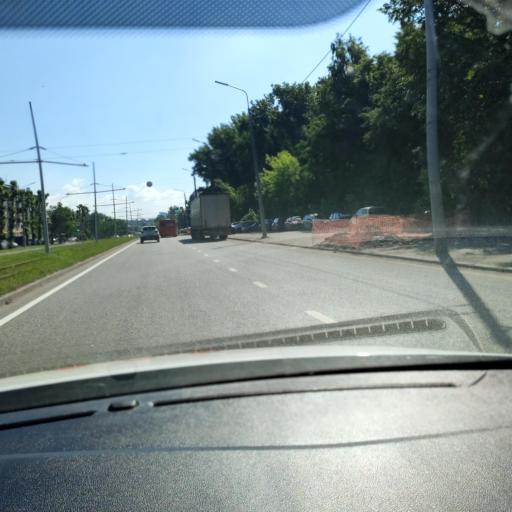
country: RU
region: Tatarstan
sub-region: Gorod Kazan'
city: Kazan
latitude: 55.7422
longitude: 49.1405
